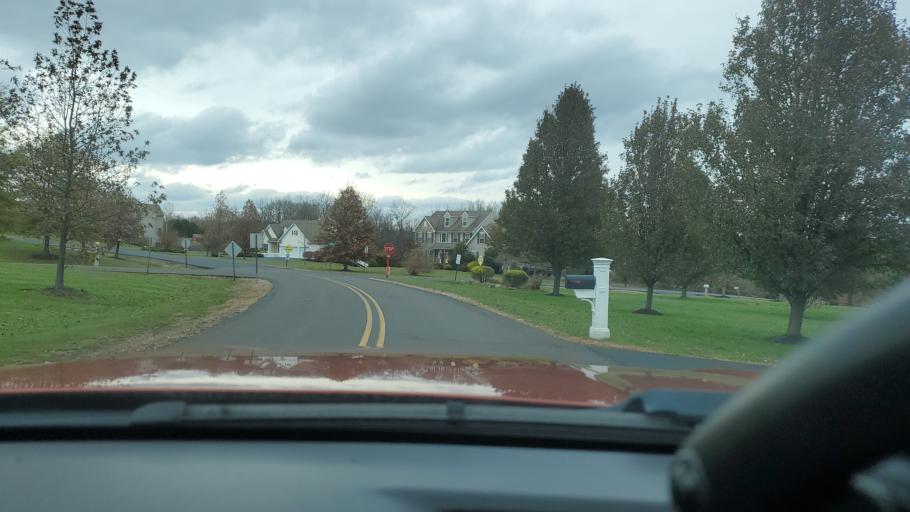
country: US
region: Pennsylvania
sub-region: Montgomery County
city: Spring Mount
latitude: 40.2866
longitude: -75.5050
